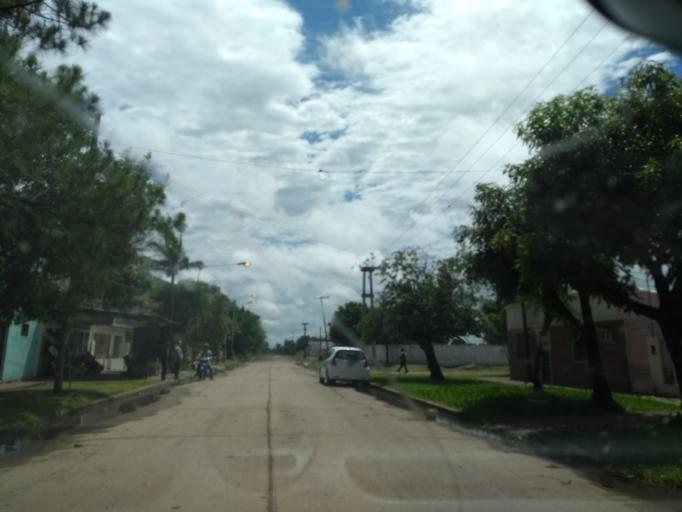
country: AR
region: Chaco
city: Barranqueras
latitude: -27.4808
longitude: -58.9483
